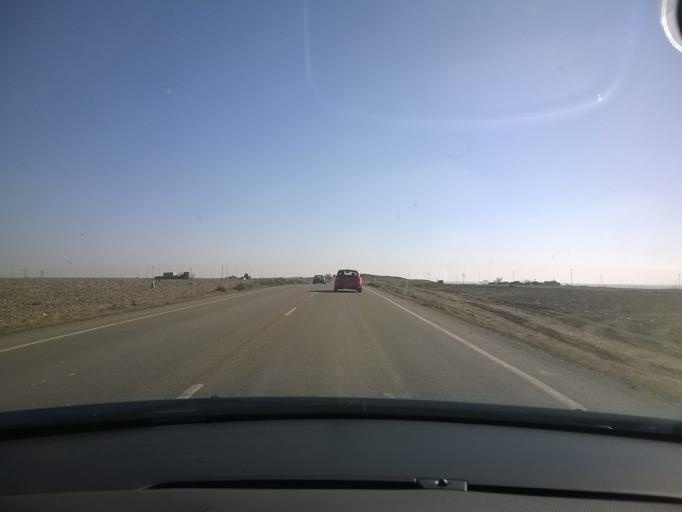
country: ES
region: Aragon
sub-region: Provincia de Zaragoza
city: Bujaraloz
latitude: 41.5169
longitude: -0.1733
